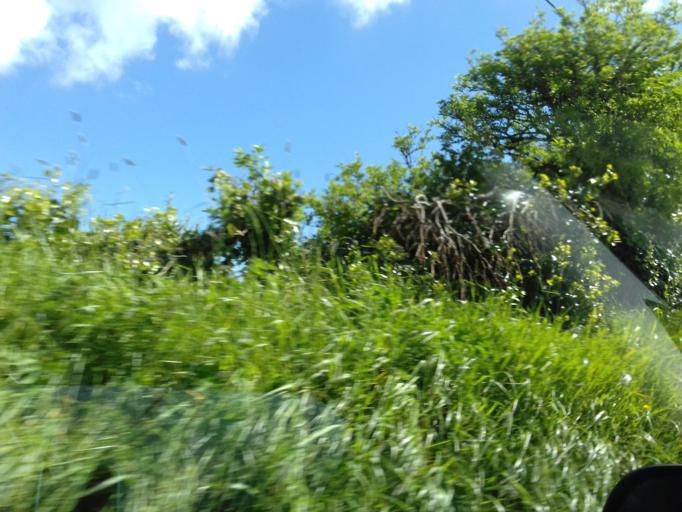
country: IE
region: Leinster
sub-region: Loch Garman
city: Castlebridge
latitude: 52.3904
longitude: -6.3828
